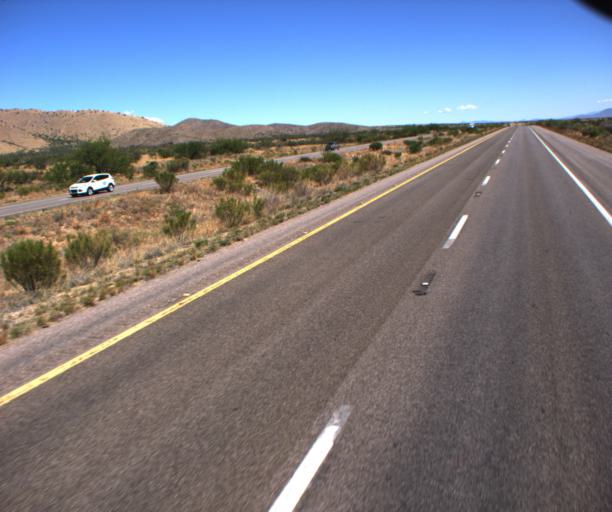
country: US
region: Arizona
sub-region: Cochise County
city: Whetstone
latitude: 31.8223
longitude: -110.3461
